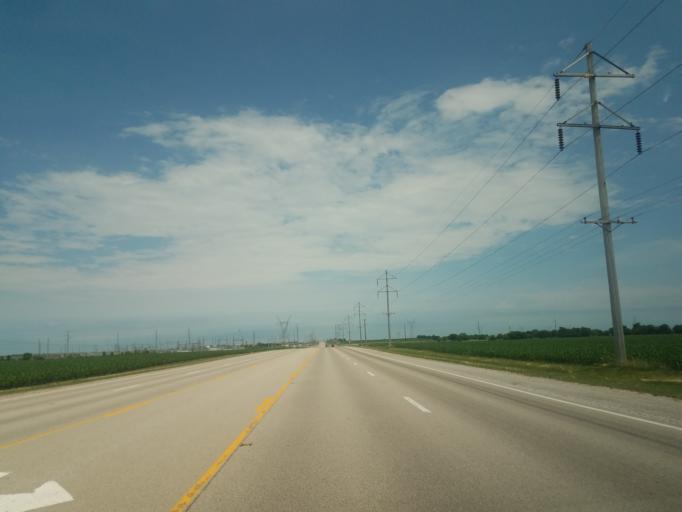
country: US
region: Illinois
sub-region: McLean County
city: Downs
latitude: 40.4456
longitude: -88.9017
